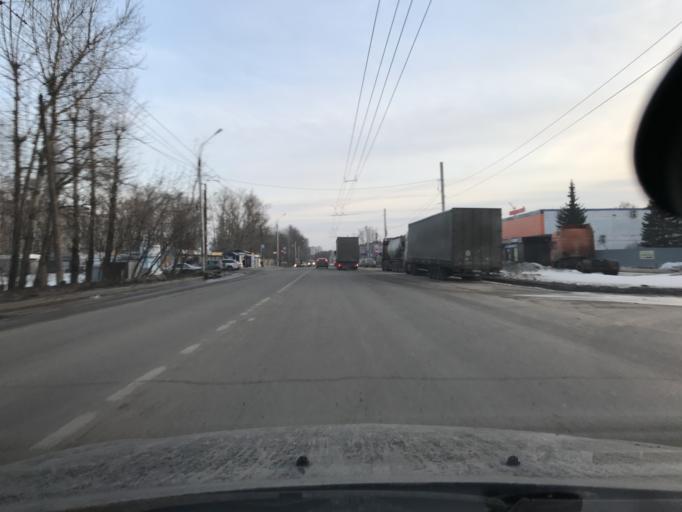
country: RU
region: Kaluga
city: Kaluga
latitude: 54.5991
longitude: 36.2615
